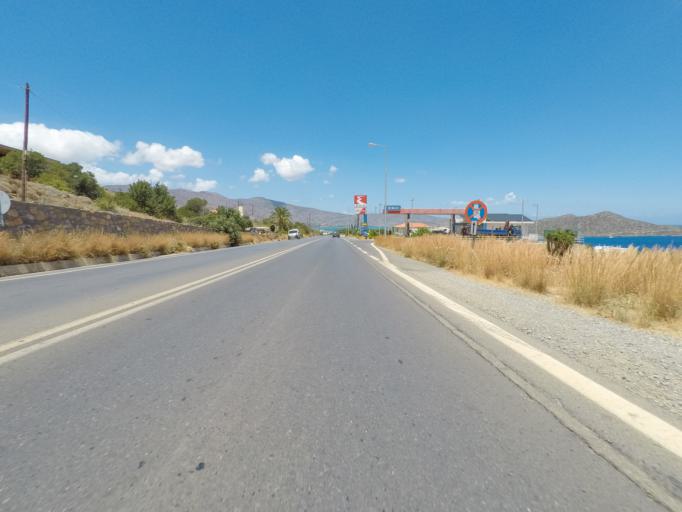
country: GR
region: Crete
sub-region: Nomos Lasithiou
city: Skhisma
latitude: 35.2426
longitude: 25.7257
